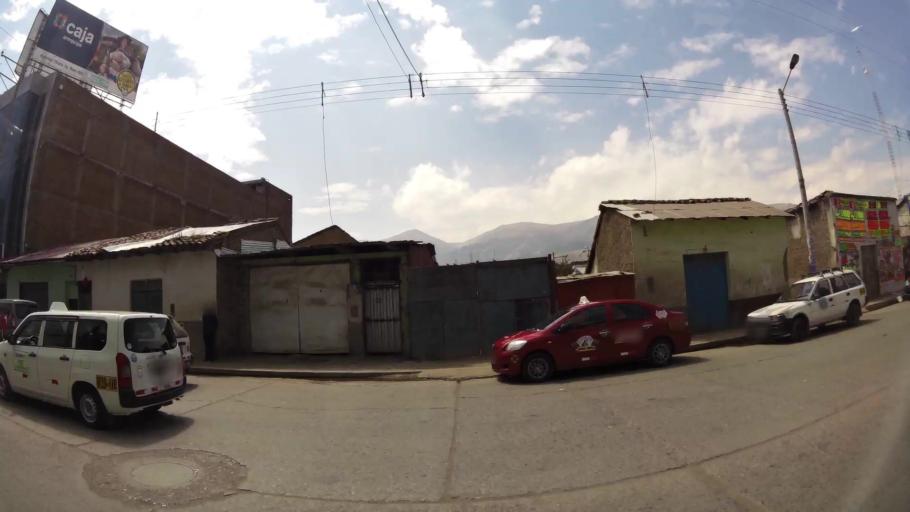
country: PE
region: Junin
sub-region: Provincia de Huancayo
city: Huancayo
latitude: -12.0813
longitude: -75.2024
